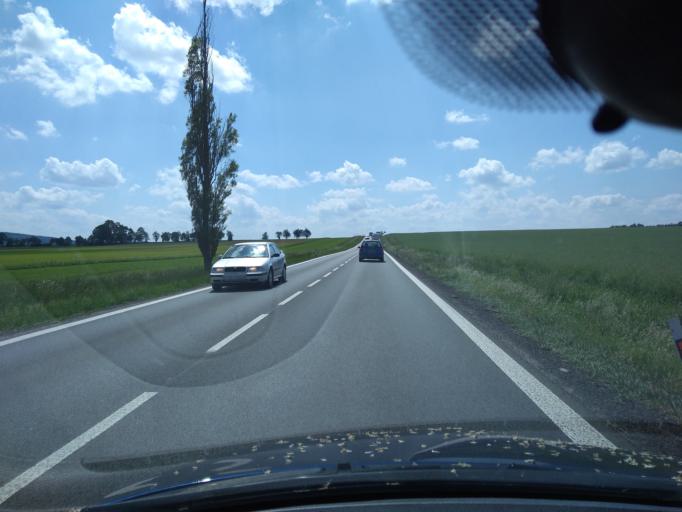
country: CZ
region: Plzensky
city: Chlumcany
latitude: 49.6047
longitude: 13.3250
